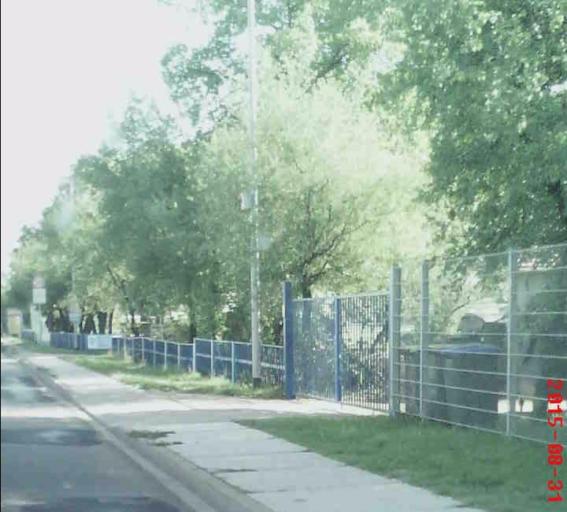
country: DE
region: Thuringia
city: Kleinmolsen
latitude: 51.0047
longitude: 11.0964
